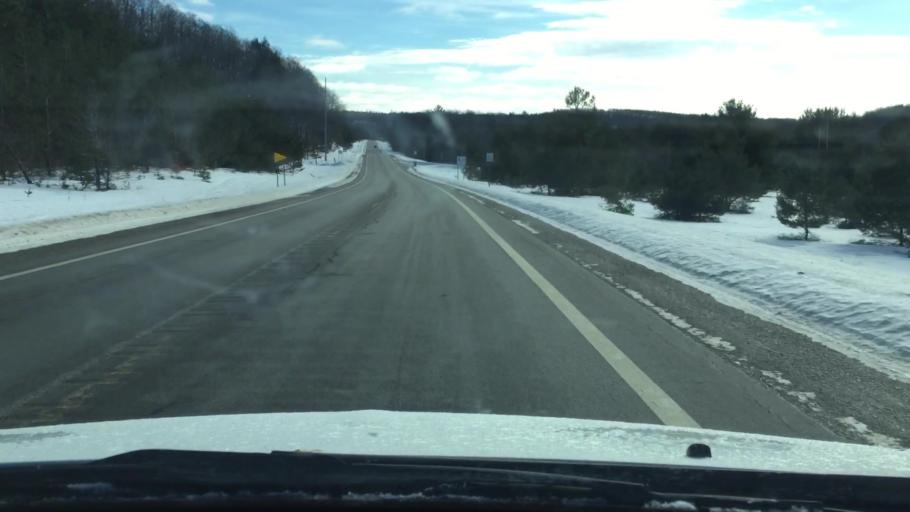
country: US
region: Michigan
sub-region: Antrim County
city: Mancelona
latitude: 44.9695
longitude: -85.0545
